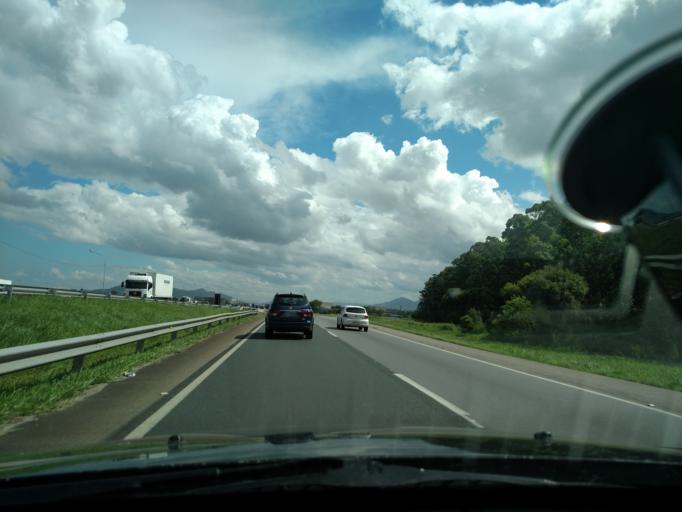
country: BR
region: Santa Catarina
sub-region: Tijucas
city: Tijucas
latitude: -27.2139
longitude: -48.6228
